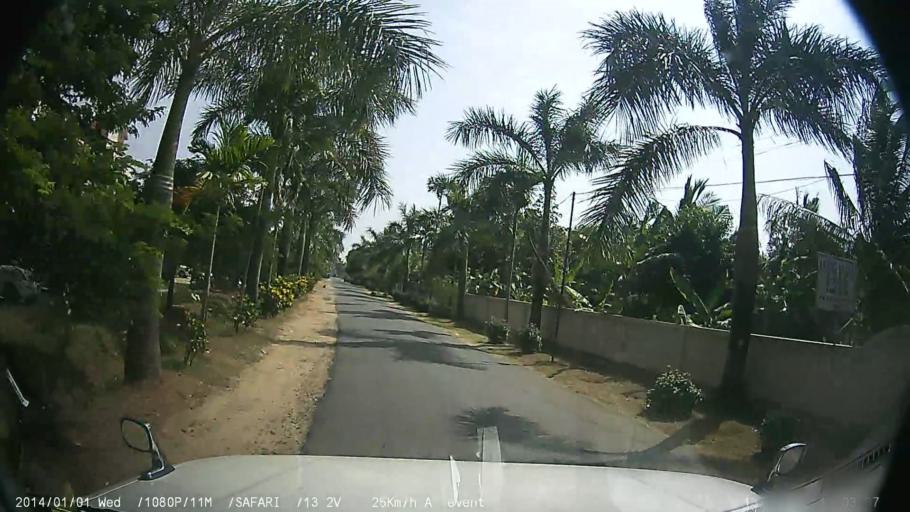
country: IN
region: Kerala
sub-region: Palakkad district
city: Palakkad
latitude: 10.7381
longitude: 76.6501
